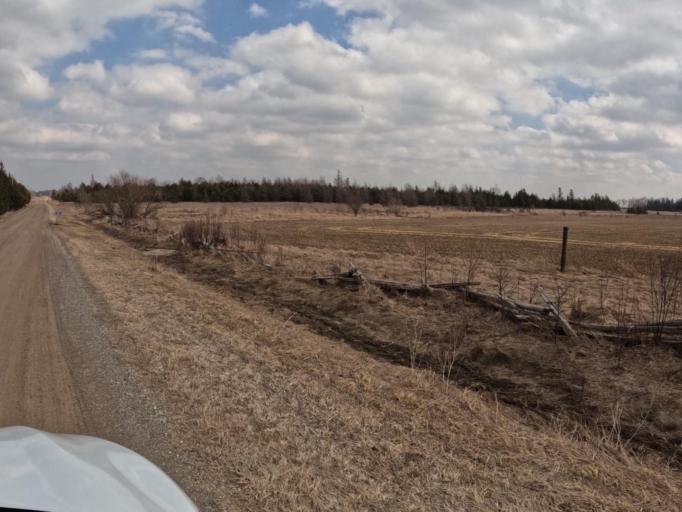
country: CA
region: Ontario
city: Shelburne
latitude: 44.0177
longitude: -80.3116
